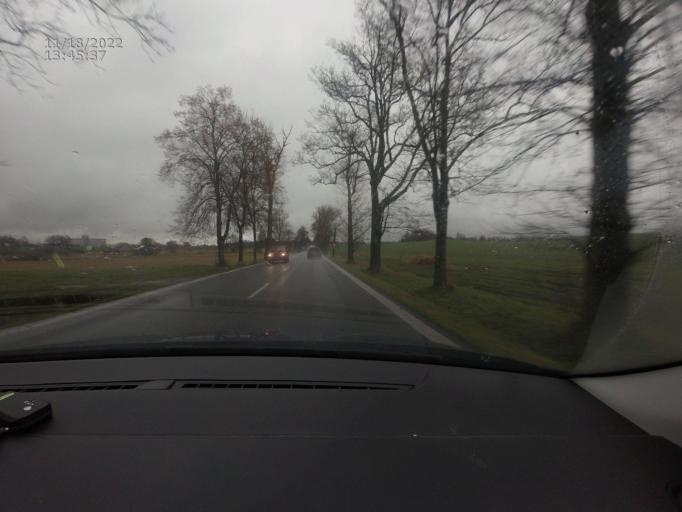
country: CZ
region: Jihocesky
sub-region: Okres Strakonice
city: Blatna
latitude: 49.4277
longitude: 13.8508
